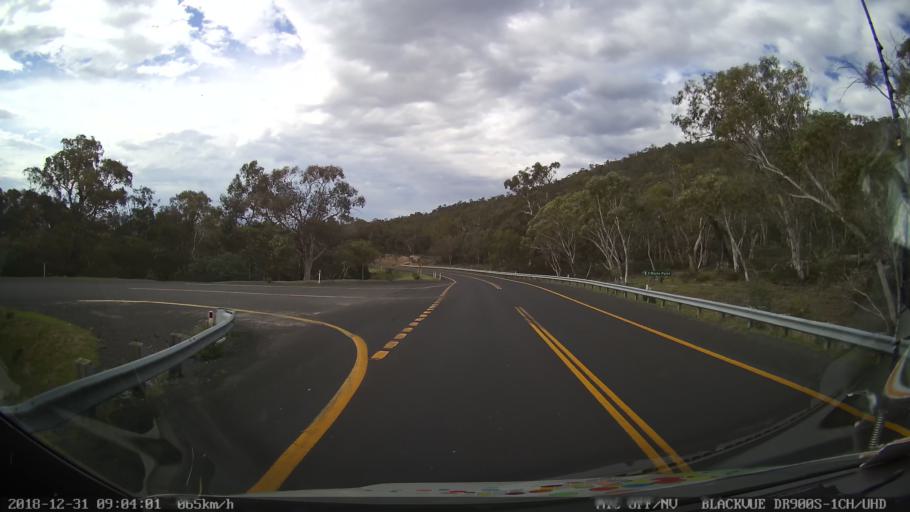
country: AU
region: New South Wales
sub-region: Snowy River
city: Jindabyne
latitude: -36.3499
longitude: 148.5855
